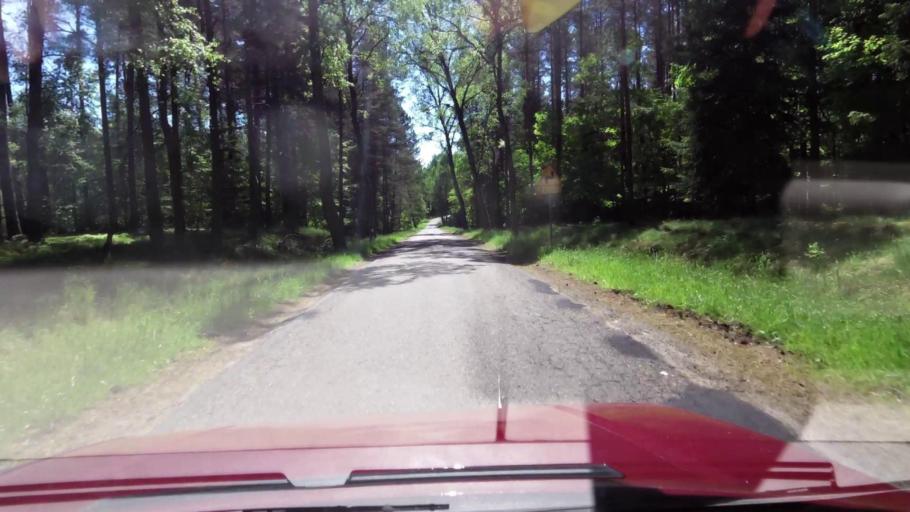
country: PL
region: West Pomeranian Voivodeship
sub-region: Powiat koszalinski
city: Bobolice
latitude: 54.0630
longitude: 16.5681
